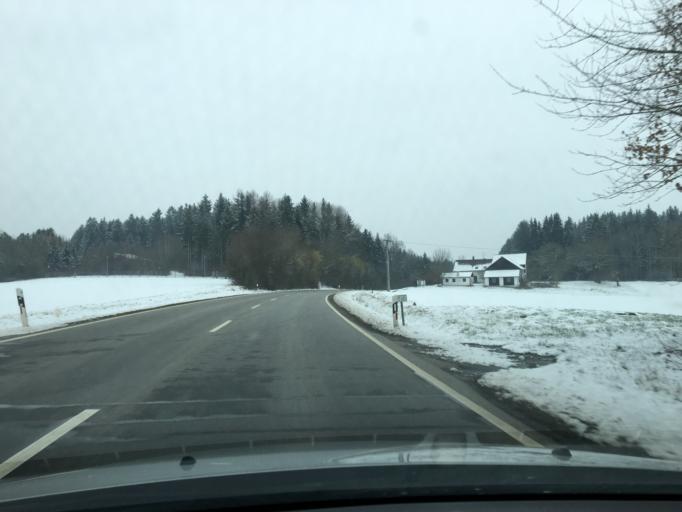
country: DE
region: Bavaria
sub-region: Lower Bavaria
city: Furth
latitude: 48.4337
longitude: 12.3819
